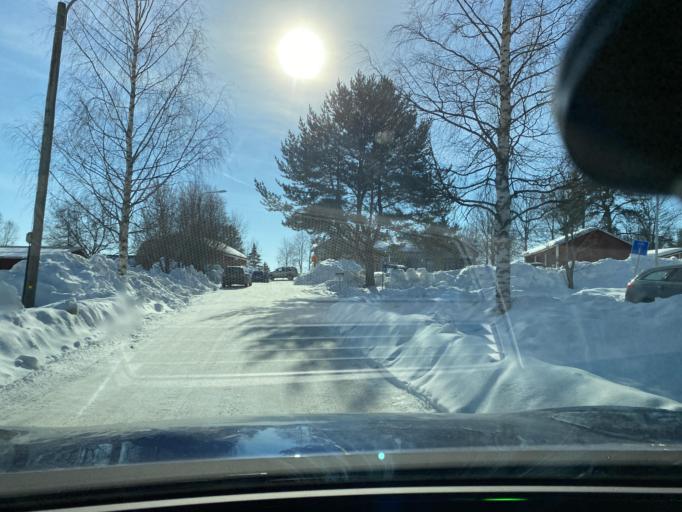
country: FI
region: Central Finland
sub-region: Jyvaeskylae
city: Korpilahti
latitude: 62.0164
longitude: 25.5691
